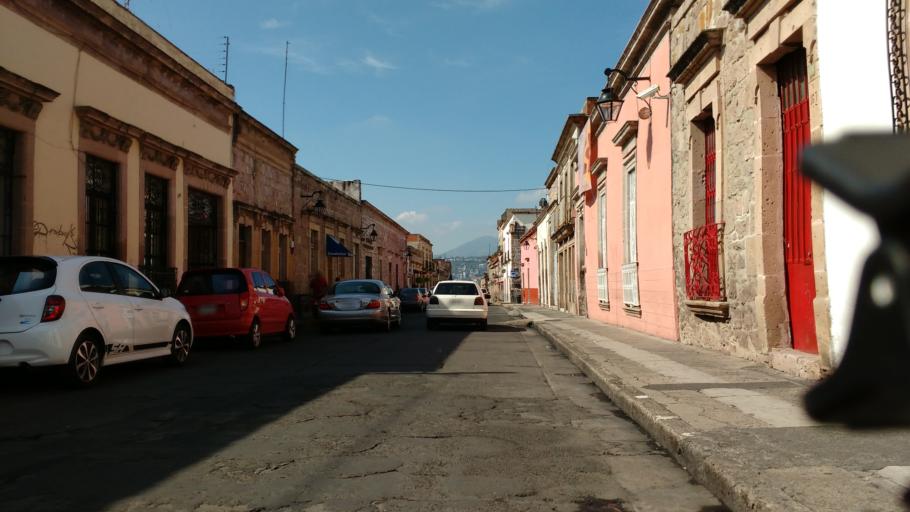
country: MX
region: Michoacan
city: Morelia
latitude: 19.7044
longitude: -101.1865
